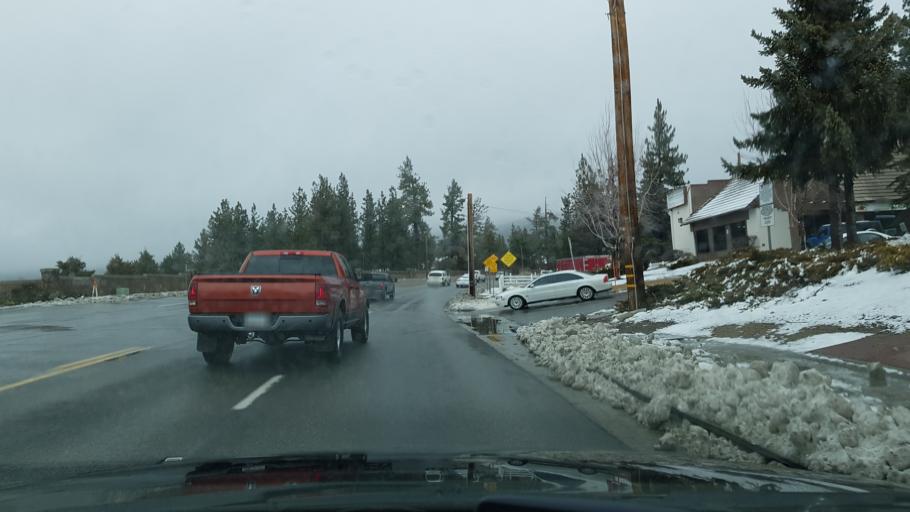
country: US
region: California
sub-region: San Bernardino County
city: Big Bear Lake
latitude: 34.2532
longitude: -116.8846
